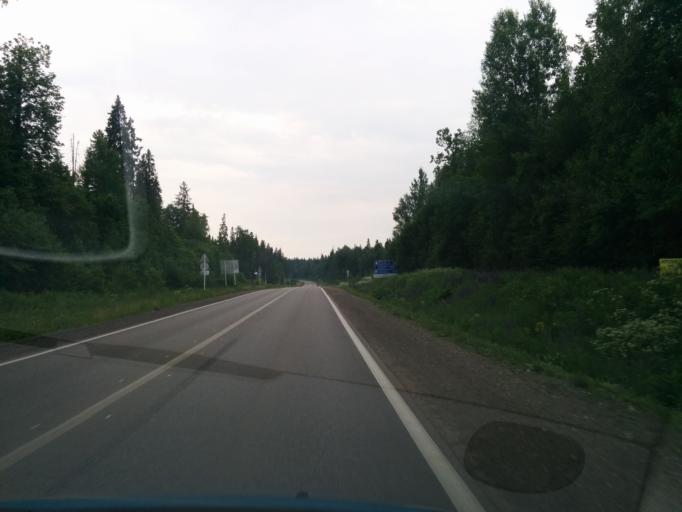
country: RU
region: Perm
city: Perm
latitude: 58.1957
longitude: 56.2104
